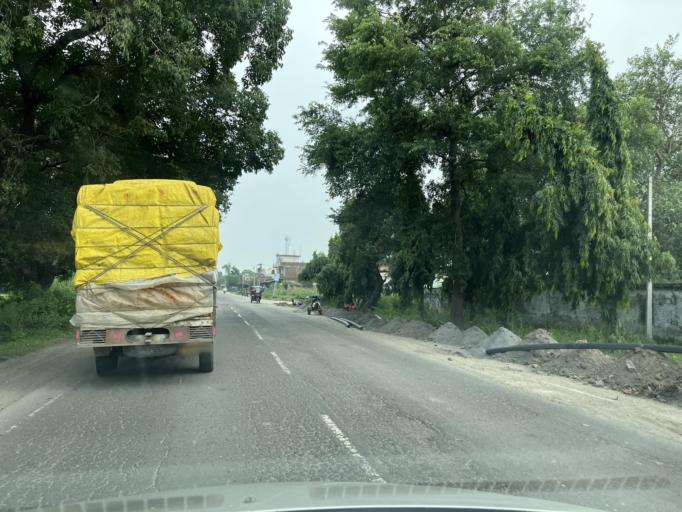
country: IN
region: Uttar Pradesh
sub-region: Rampur
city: Bilaspur
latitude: 29.0332
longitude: 79.2596
